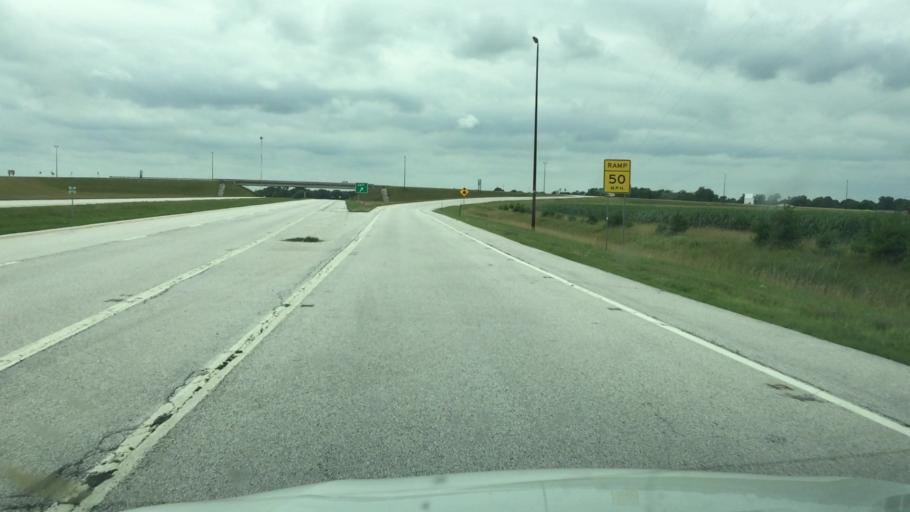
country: US
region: Illinois
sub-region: Hancock County
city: Carthage
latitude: 40.4149
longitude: -91.1088
